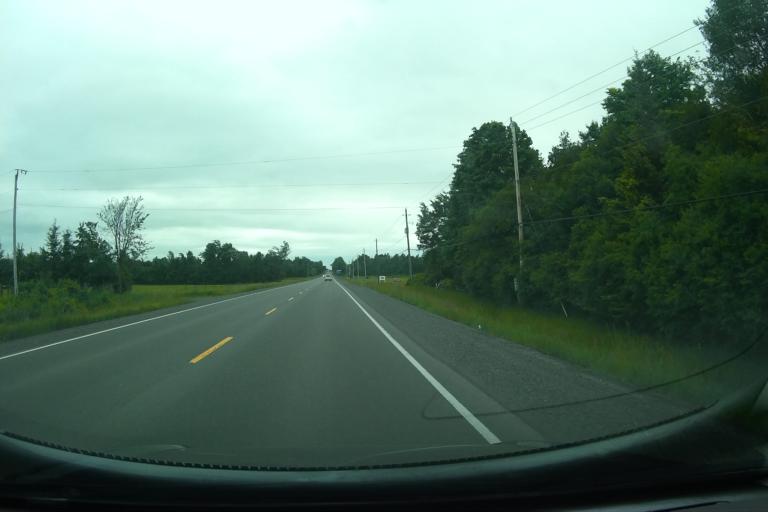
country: CA
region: Ontario
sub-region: Lanark County
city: Smiths Falls
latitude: 44.9636
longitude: -75.7624
